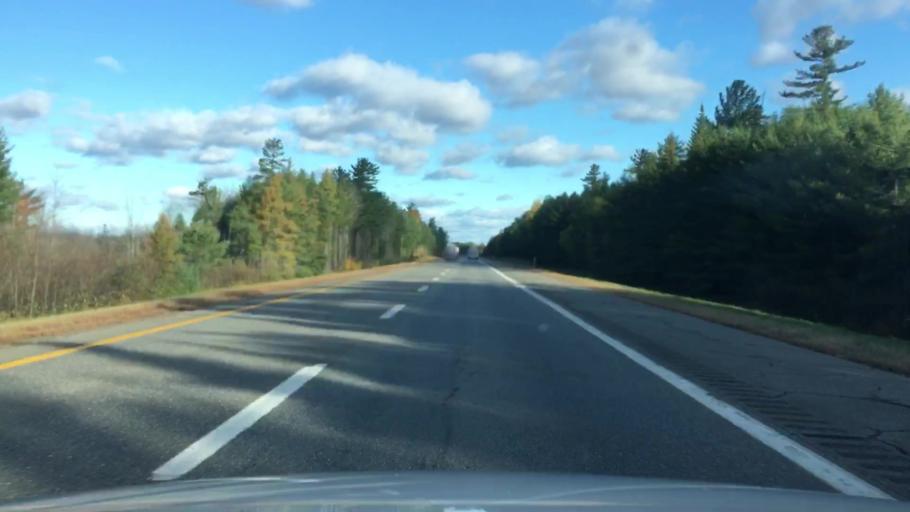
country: US
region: Maine
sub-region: Penobscot County
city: Greenbush
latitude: 45.1347
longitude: -68.6983
